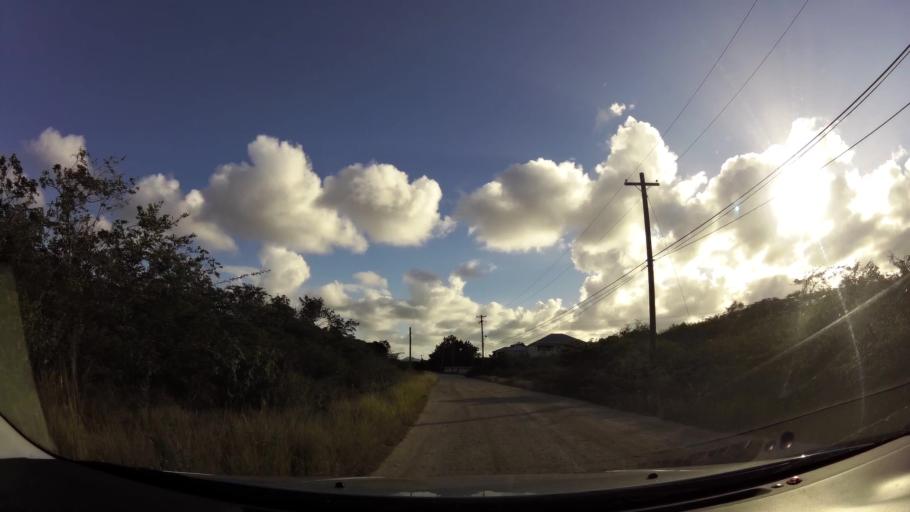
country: AG
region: Saint George
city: Piggotts
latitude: 17.1183
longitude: -61.7892
